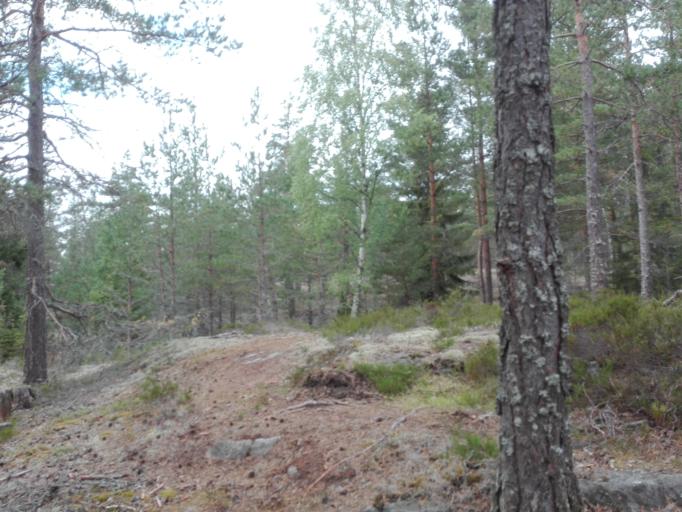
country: SE
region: Stockholm
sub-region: Nacka Kommun
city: Fisksatra
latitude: 59.2800
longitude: 18.2489
